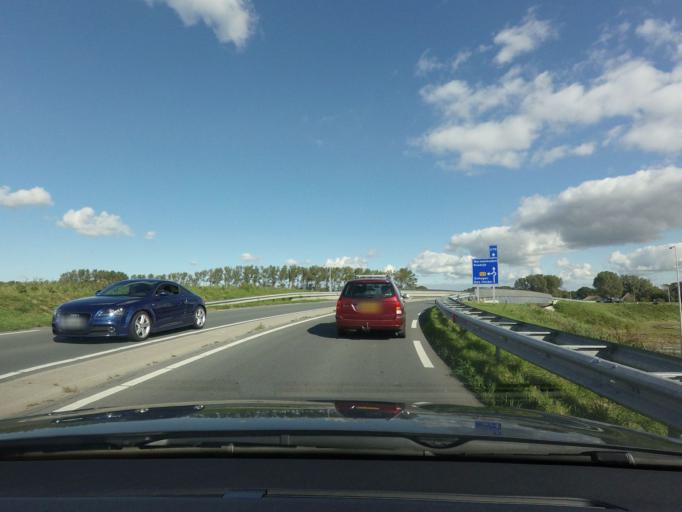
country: NL
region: North Holland
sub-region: Gemeente Schagen
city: Harenkarspel
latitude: 52.7086
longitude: 4.7126
